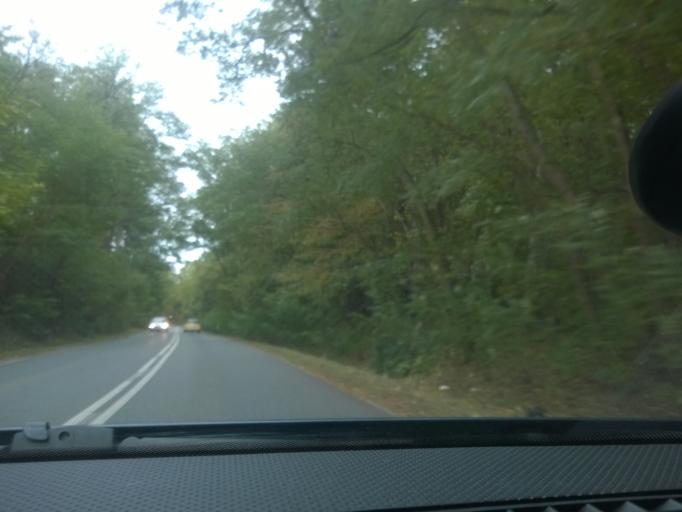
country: PL
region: Masovian Voivodeship
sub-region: Powiat pruszkowski
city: Granica
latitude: 52.1233
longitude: 20.7982
